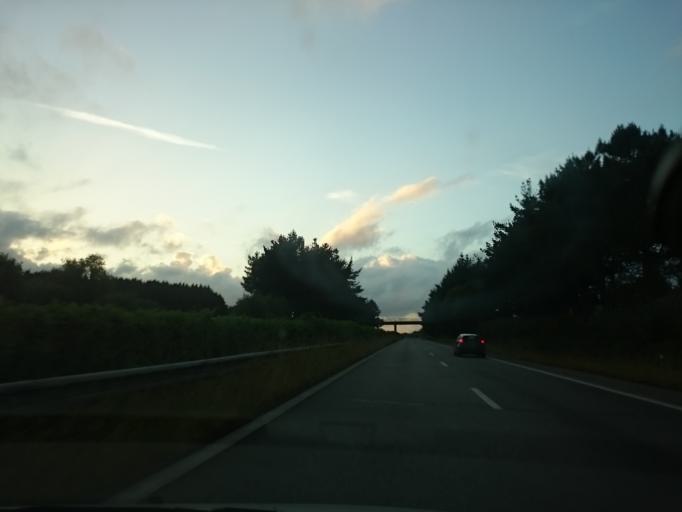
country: FR
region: Brittany
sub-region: Departement du Morbihan
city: Gestel
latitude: 47.8043
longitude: -3.4582
